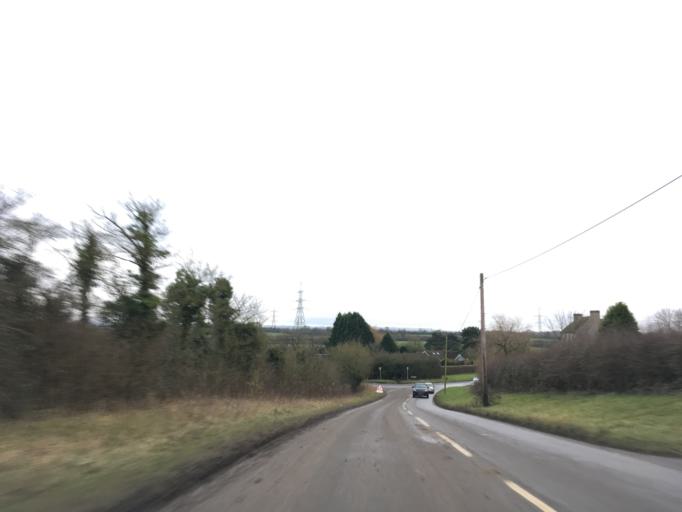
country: GB
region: England
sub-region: South Gloucestershire
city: Winterbourne
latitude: 51.5515
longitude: -2.5136
